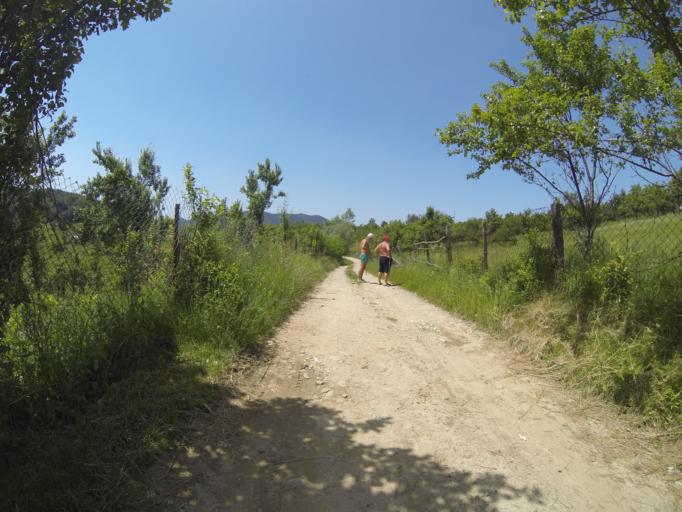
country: RO
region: Valcea
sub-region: Oras Baile Olanesti
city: Baile Olanesti
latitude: 45.2045
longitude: 24.2157
